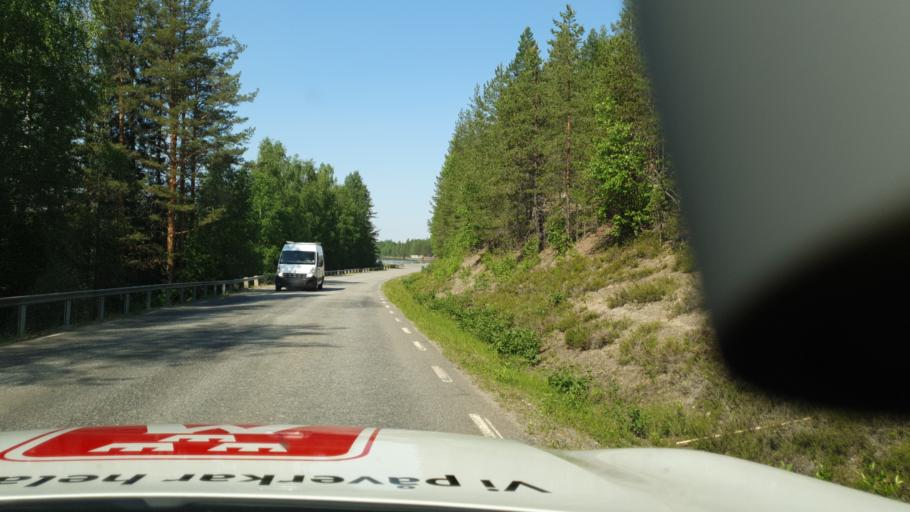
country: SE
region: Vaesterbotten
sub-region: Skelleftea Kommun
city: Langsele
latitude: 64.9618
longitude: 19.8930
